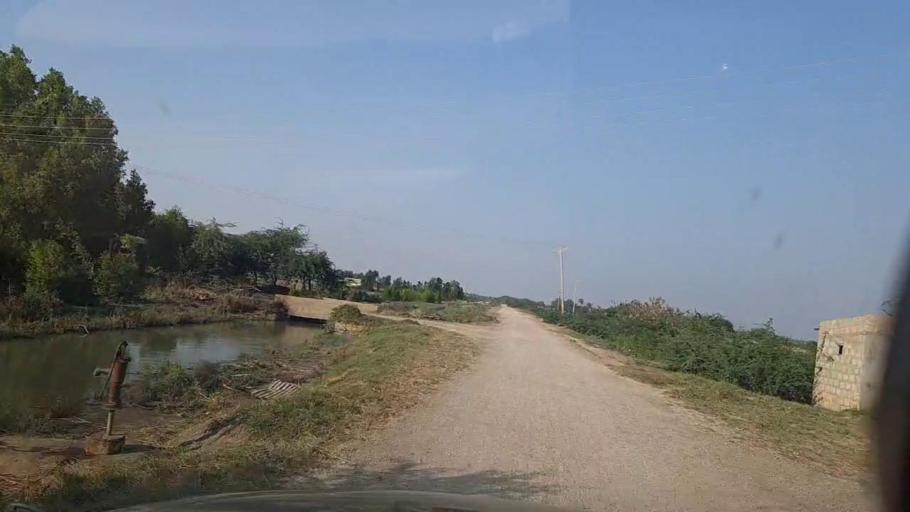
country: PK
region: Sindh
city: Thatta
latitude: 24.6125
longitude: 67.8763
